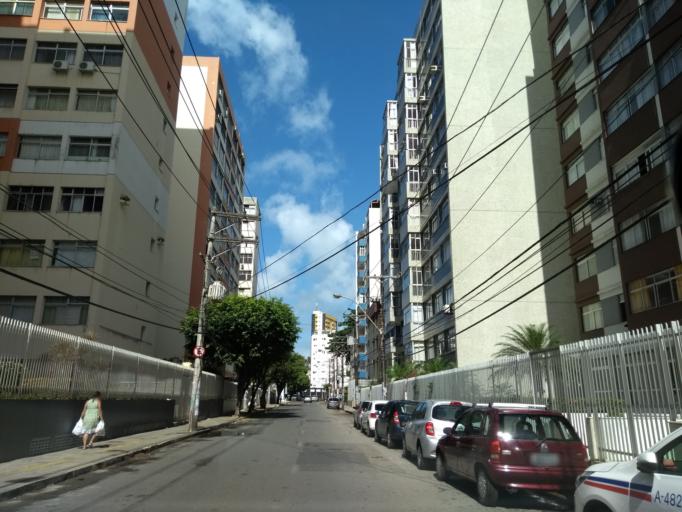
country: BR
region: Bahia
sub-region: Salvador
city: Salvador
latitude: -13.0054
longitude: -38.5244
